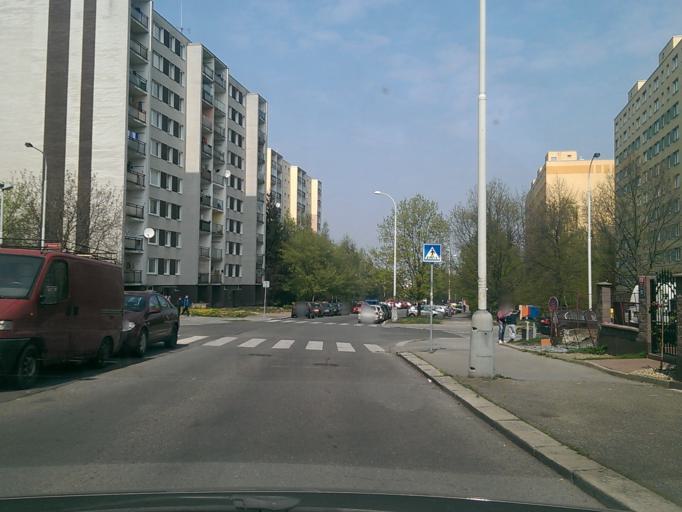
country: CZ
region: Central Bohemia
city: Vestec
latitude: 50.0358
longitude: 14.5011
